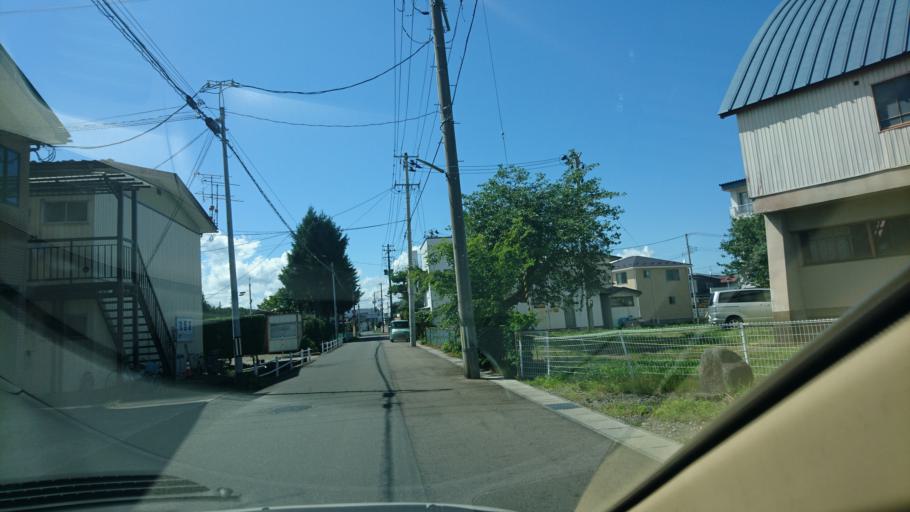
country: JP
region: Iwate
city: Kitakami
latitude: 39.2878
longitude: 141.1077
